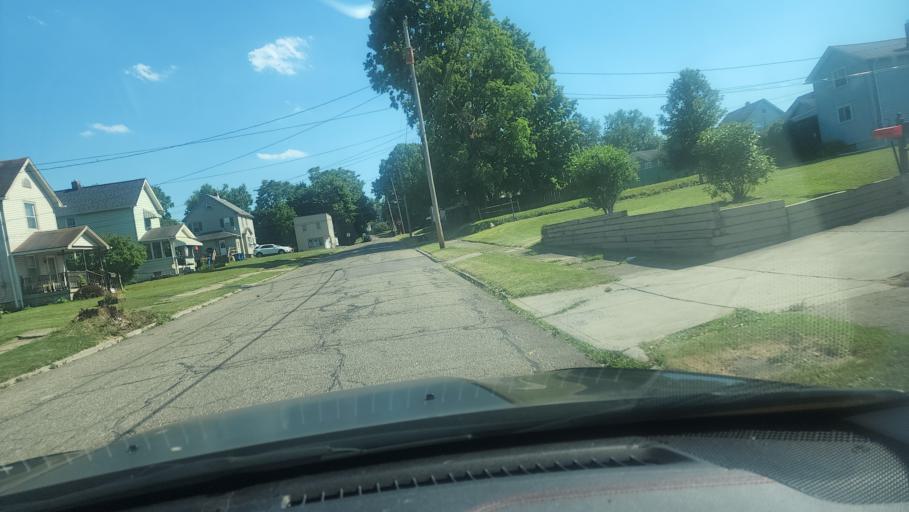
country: US
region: Ohio
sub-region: Mahoning County
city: Struthers
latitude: 41.0569
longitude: -80.6063
